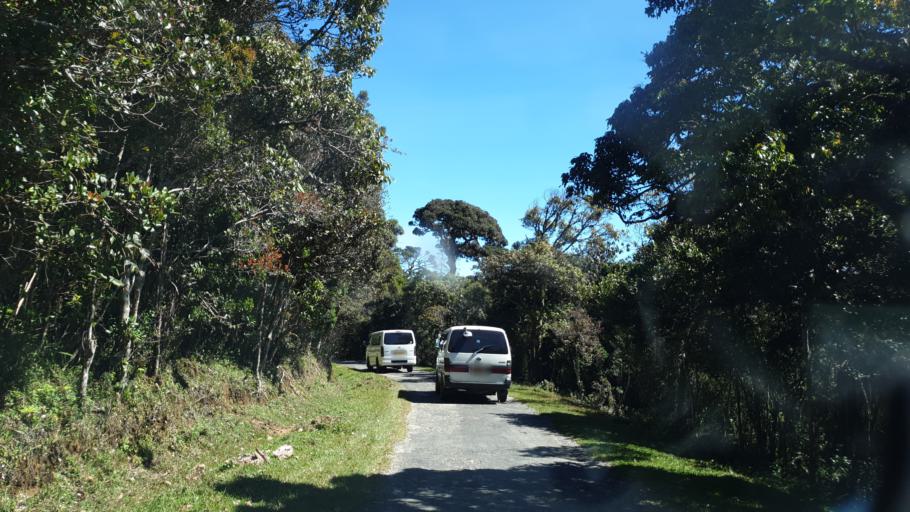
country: LK
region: Uva
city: Haputale
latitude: 6.7984
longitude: 80.8315
